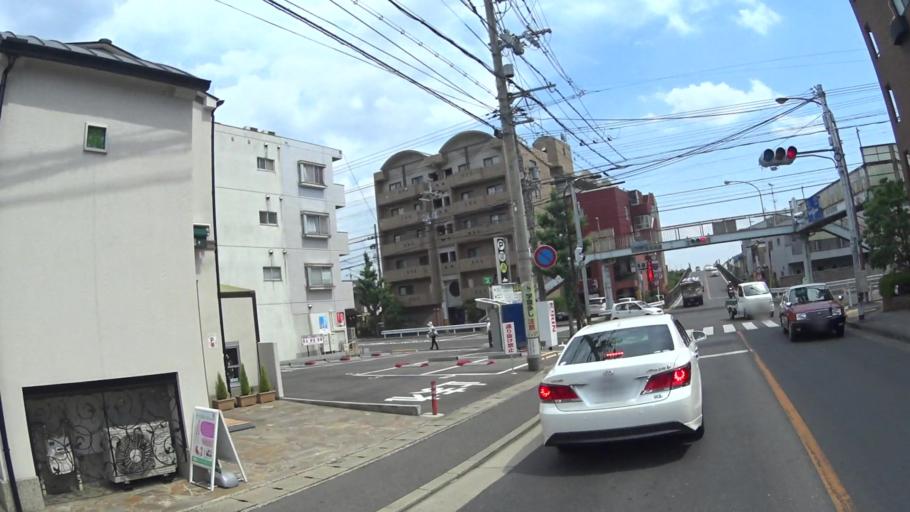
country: JP
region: Kyoto
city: Muko
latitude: 35.0204
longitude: 135.6777
